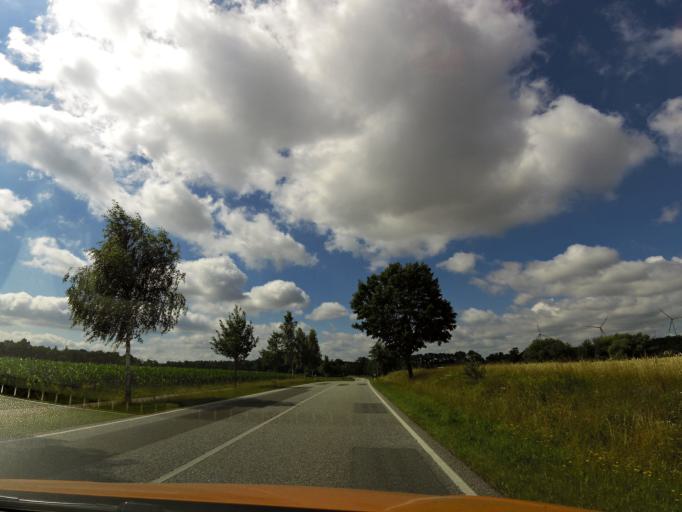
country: DE
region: Mecklenburg-Vorpommern
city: Plau am See
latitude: 53.5098
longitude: 12.2689
